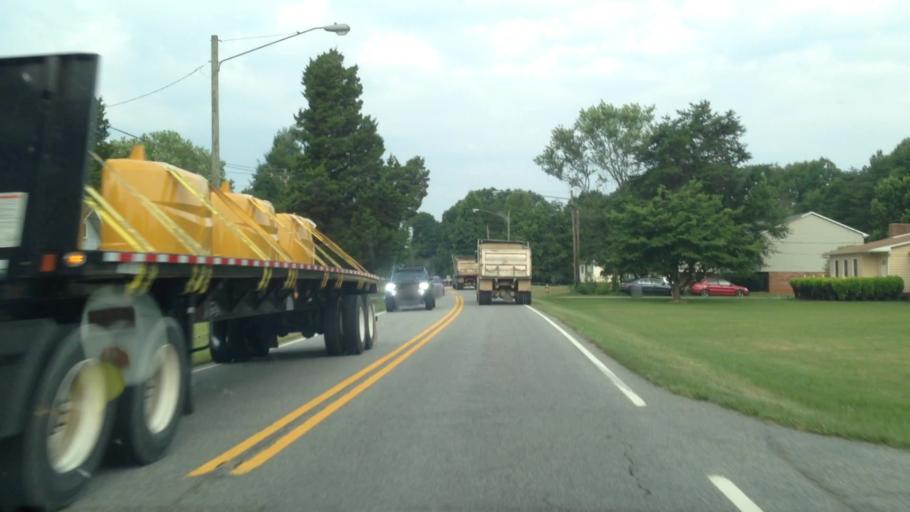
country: US
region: North Carolina
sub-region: Forsyth County
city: Rural Hall
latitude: 36.1920
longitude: -80.2378
